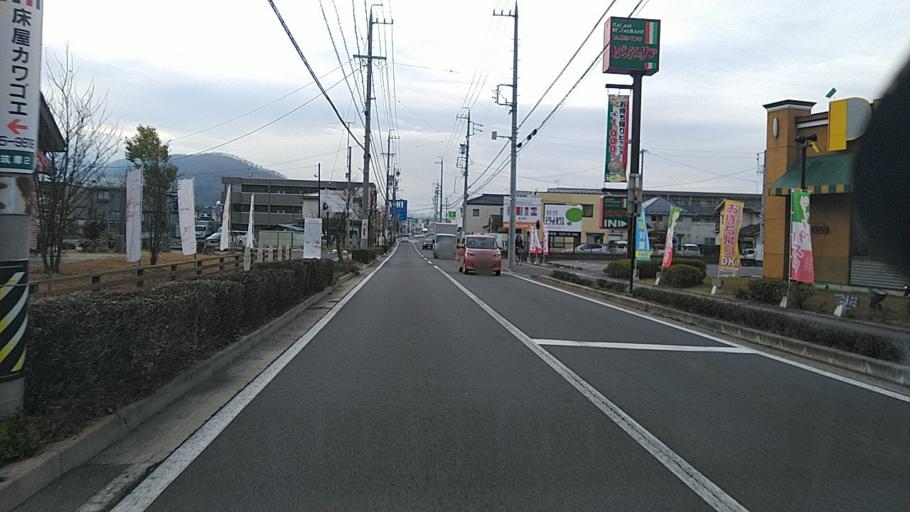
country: JP
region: Nagano
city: Matsumoto
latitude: 36.2241
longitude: 137.9797
